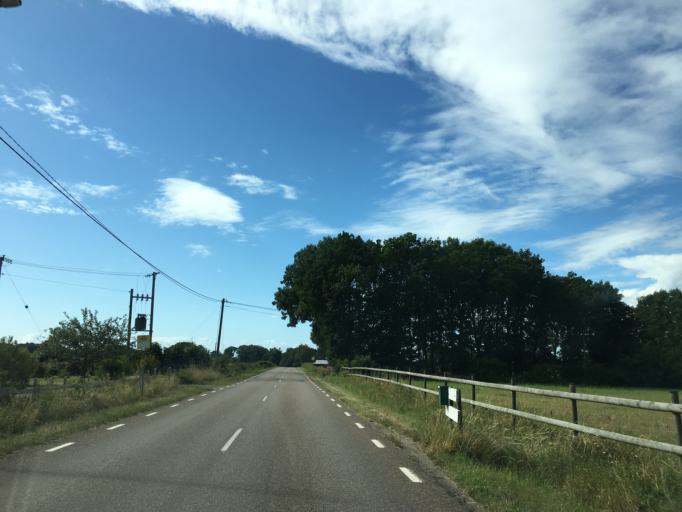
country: SE
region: Kalmar
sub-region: Morbylanga Kommun
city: Moerbylanga
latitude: 56.4261
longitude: 16.4170
